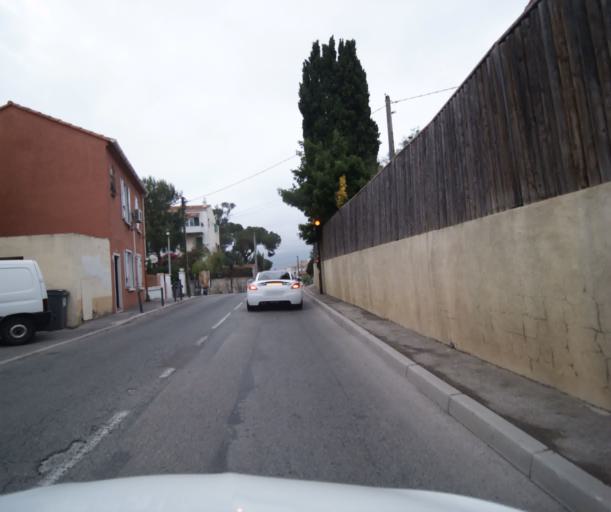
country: FR
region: Provence-Alpes-Cote d'Azur
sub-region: Departement du Var
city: La Seyne-sur-Mer
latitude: 43.0956
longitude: 5.8886
